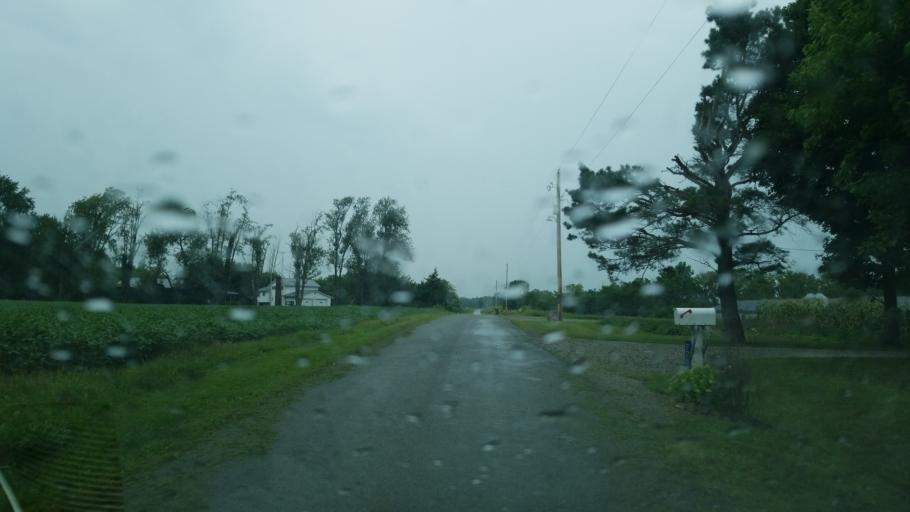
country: US
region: Ohio
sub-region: Richland County
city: Shelby
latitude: 40.9310
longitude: -82.7680
